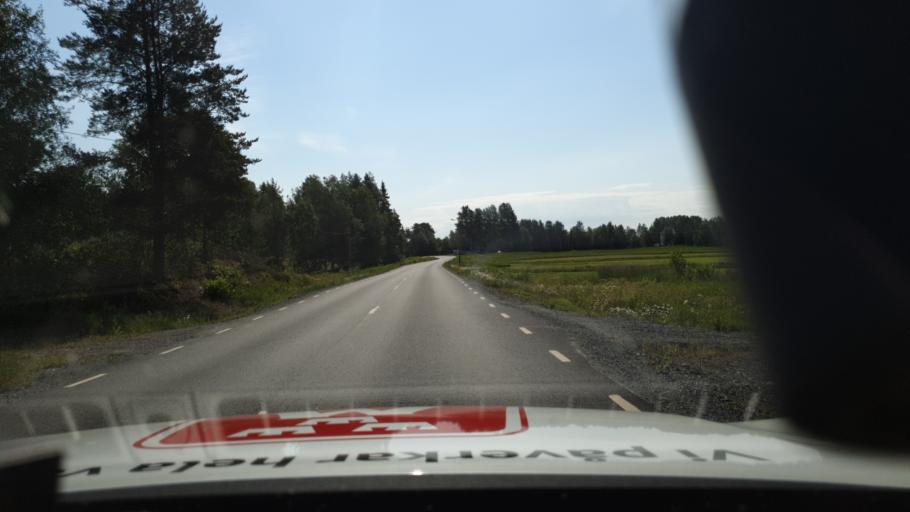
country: SE
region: Norrbotten
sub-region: Lulea Kommun
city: Sodra Sunderbyn
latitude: 65.8262
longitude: 21.9760
